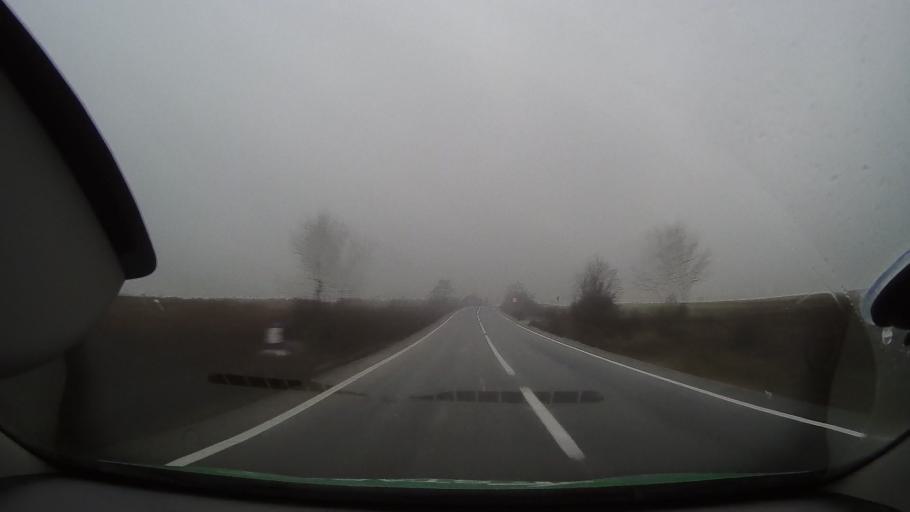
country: RO
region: Bihor
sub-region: Comuna Olcea
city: Calacea
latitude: 46.6466
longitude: 21.9575
